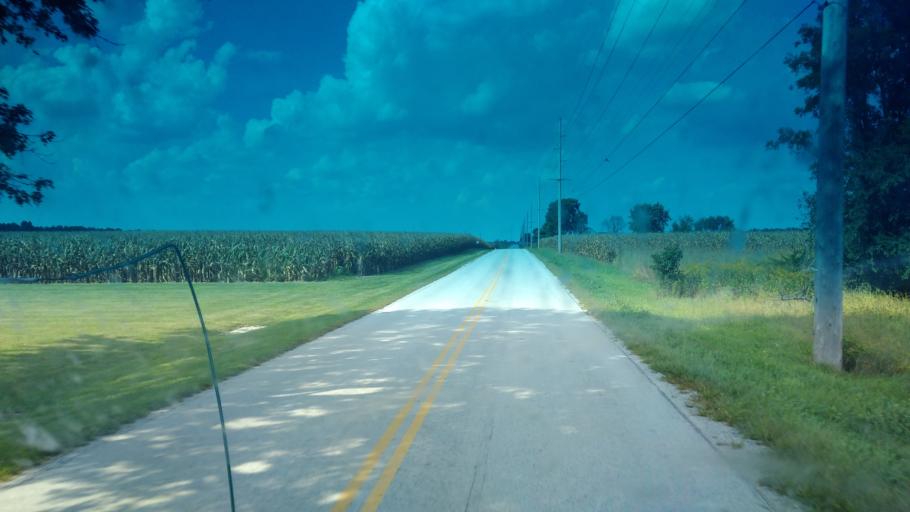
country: US
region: Ohio
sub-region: Hardin County
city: Kenton
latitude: 40.7574
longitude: -83.6524
